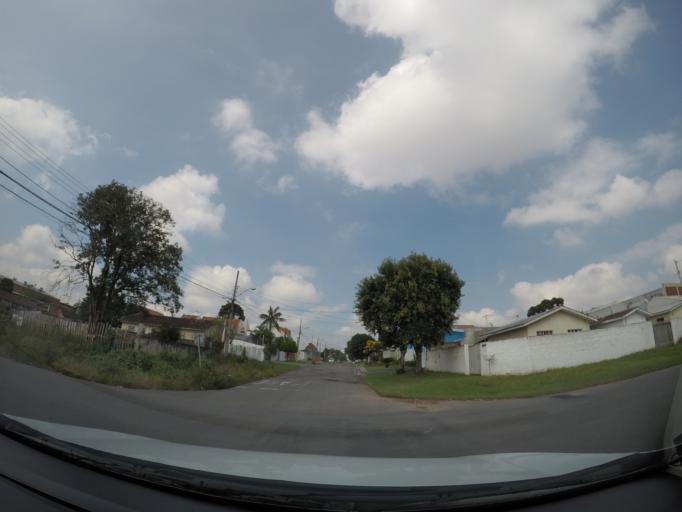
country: BR
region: Parana
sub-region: Curitiba
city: Curitiba
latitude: -25.4802
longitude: -49.2590
